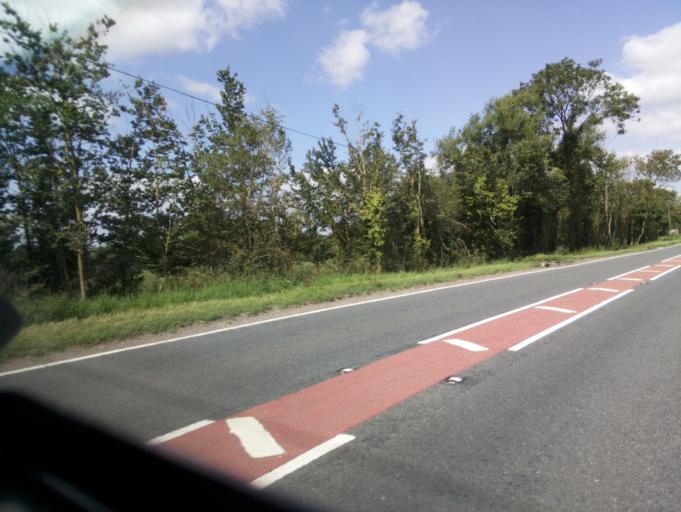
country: GB
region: England
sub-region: Buckinghamshire
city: Aylesbury
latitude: 51.8426
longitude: -0.8205
